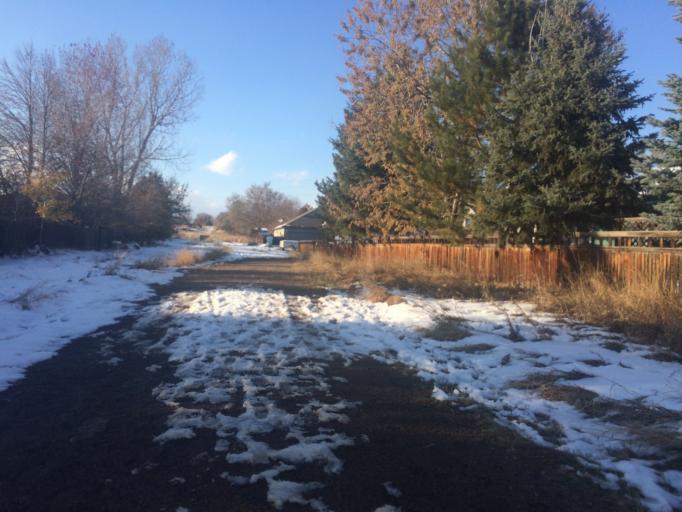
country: US
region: Colorado
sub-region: Boulder County
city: Lafayette
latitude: 39.9897
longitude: -105.1103
